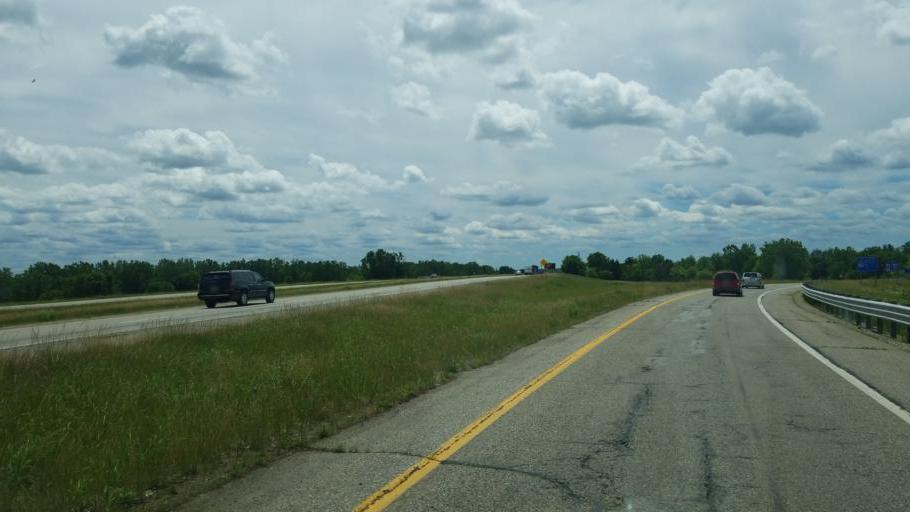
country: US
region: Michigan
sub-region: Eaton County
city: Charlotte
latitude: 42.5789
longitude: -84.8189
